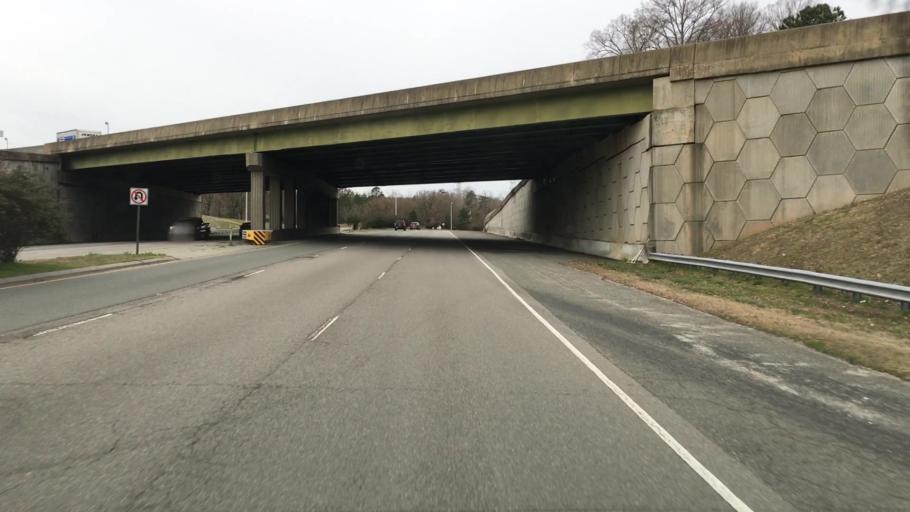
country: US
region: Virginia
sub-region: Chesterfield County
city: Bon Air
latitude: 37.5457
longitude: -77.5524
